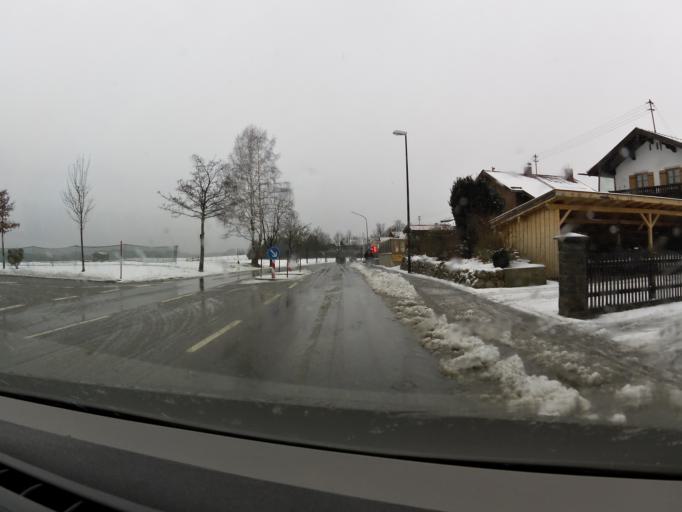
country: DE
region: Bavaria
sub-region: Upper Bavaria
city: Waakirchen
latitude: 47.7688
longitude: 11.6810
